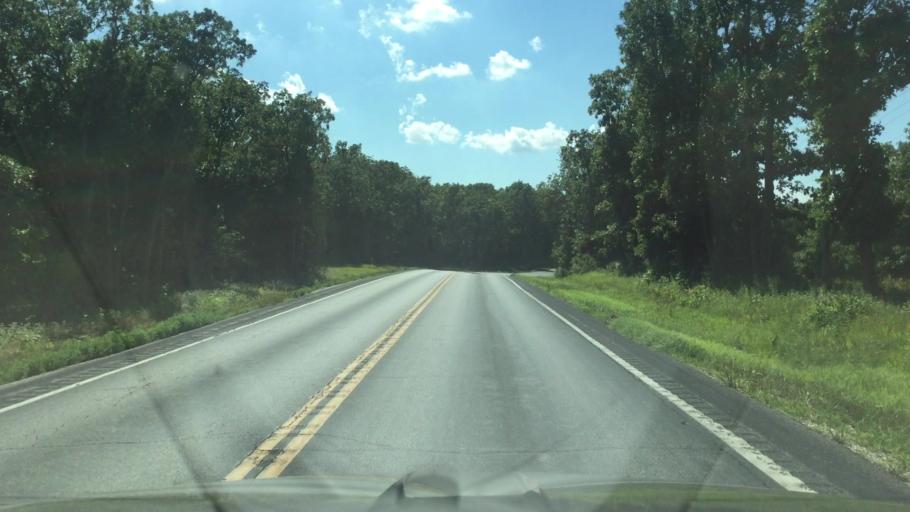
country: US
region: Missouri
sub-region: Camden County
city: Osage Beach
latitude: 38.1340
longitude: -92.5633
